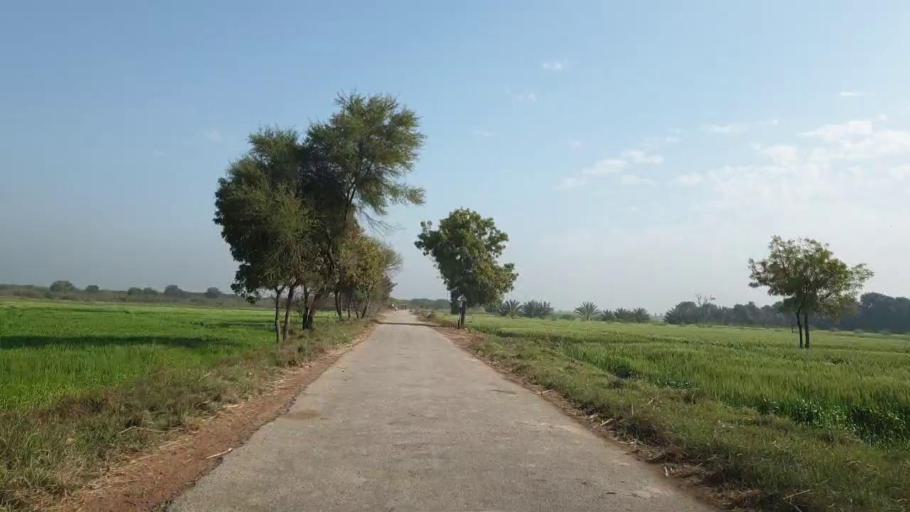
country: PK
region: Sindh
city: Matiari
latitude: 25.5961
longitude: 68.4883
